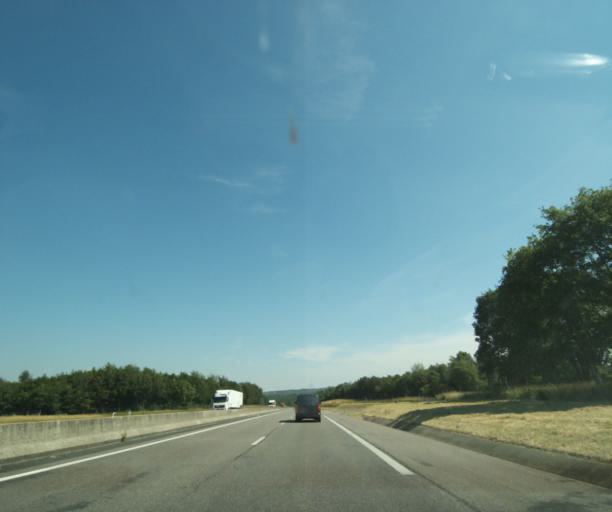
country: FR
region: Lorraine
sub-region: Departement de Meurthe-et-Moselle
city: Colombey-les-Belles
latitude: 48.4480
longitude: 5.8674
